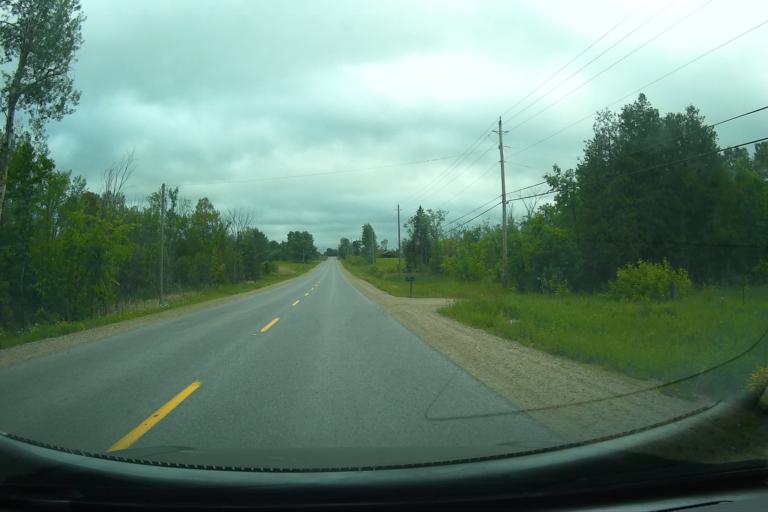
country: CA
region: Ontario
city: Pembroke
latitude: 45.4982
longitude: -77.1500
